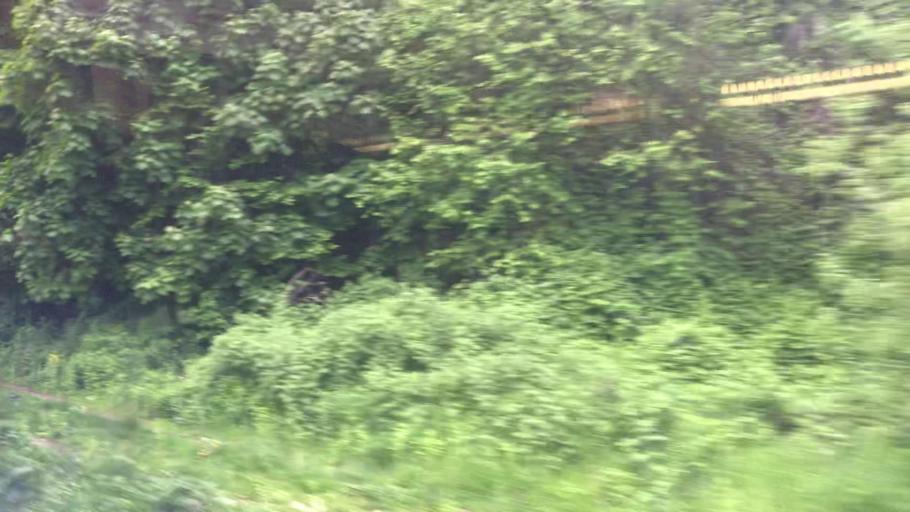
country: PL
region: Lower Silesian Voivodeship
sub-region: Powiat walbrzyski
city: Walbrzych
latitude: 50.7969
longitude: 16.2877
